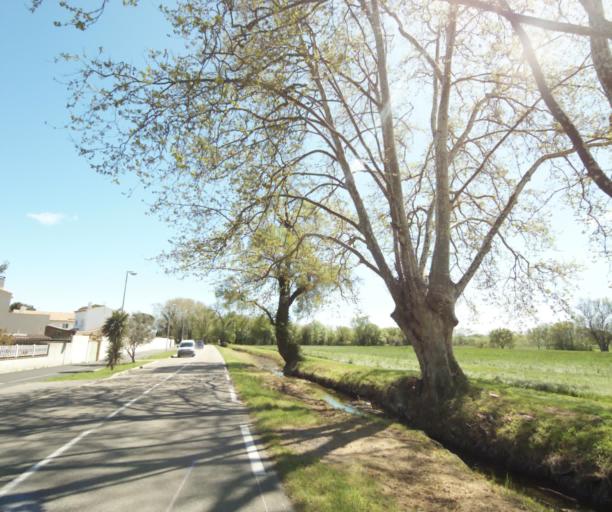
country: FR
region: Languedoc-Roussillon
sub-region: Departement de l'Herault
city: Lattes
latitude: 43.5662
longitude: 3.9109
